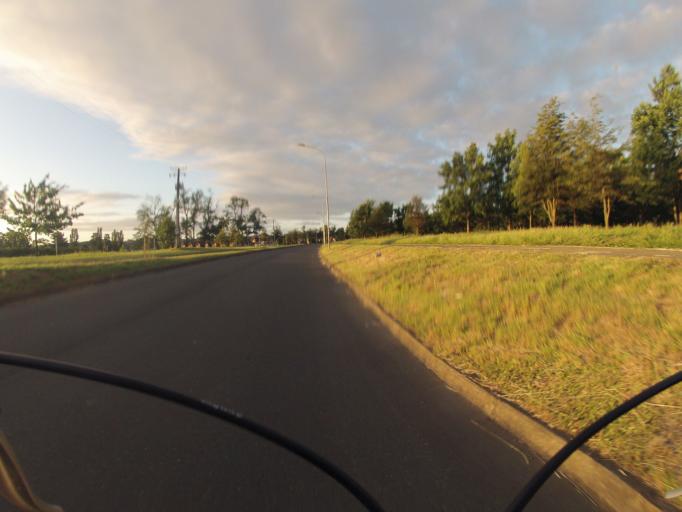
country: CL
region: Araucania
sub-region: Provincia de Cautin
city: Temuco
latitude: -38.7460
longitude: -72.6477
